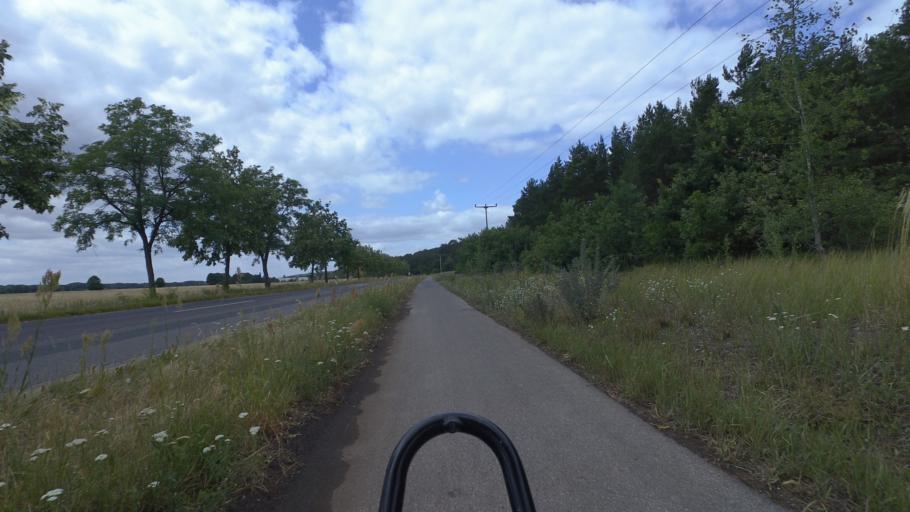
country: DE
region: Brandenburg
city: Trebbin
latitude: 52.2353
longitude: 13.1890
